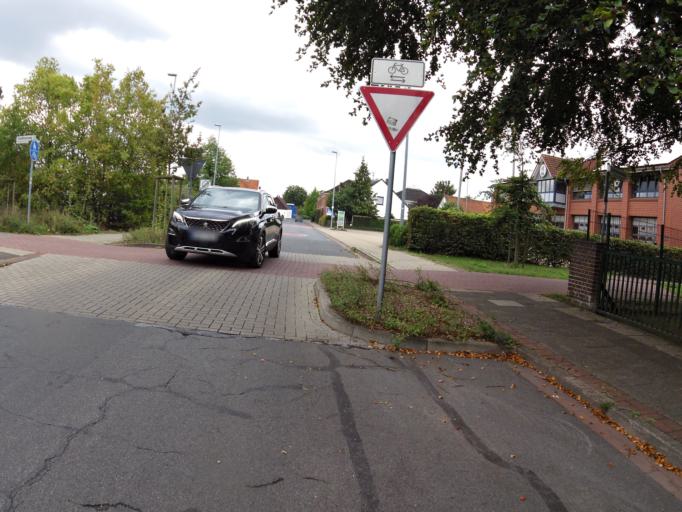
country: DE
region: Lower Saxony
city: Rotenburg
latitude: 53.1155
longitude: 9.4113
